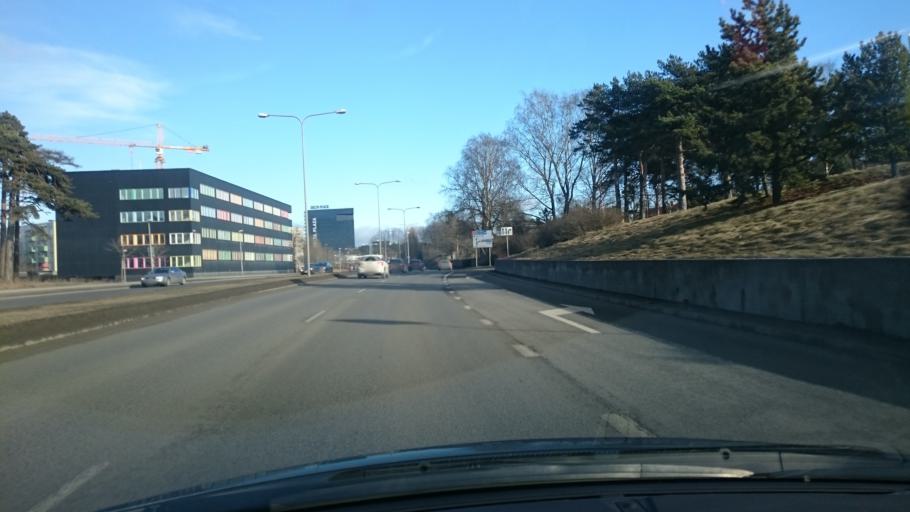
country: EE
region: Harju
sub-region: Tallinna linn
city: Tallinn
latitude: 59.4024
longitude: 24.7191
